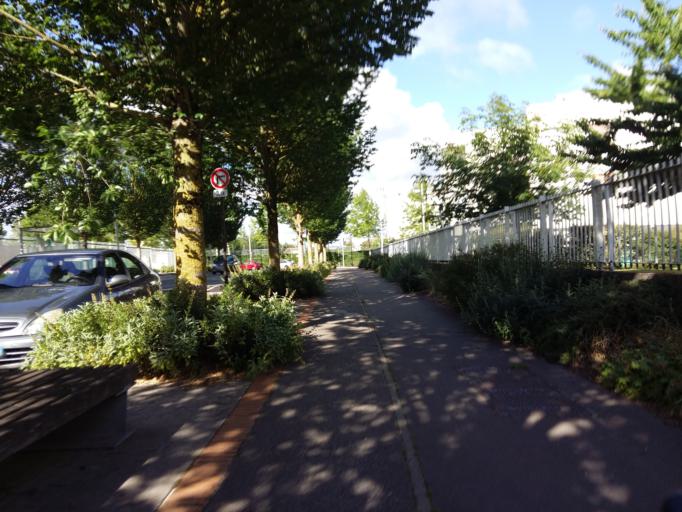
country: FR
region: Picardie
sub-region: Departement de la Somme
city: Rivery
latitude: 49.9127
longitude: 2.3107
